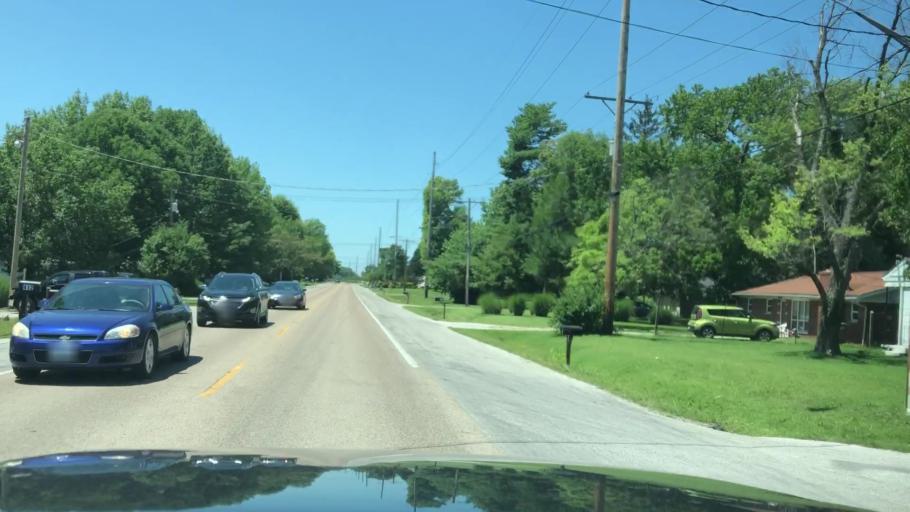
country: US
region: Illinois
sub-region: Saint Clair County
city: Centreville
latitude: 38.5449
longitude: -90.0767
